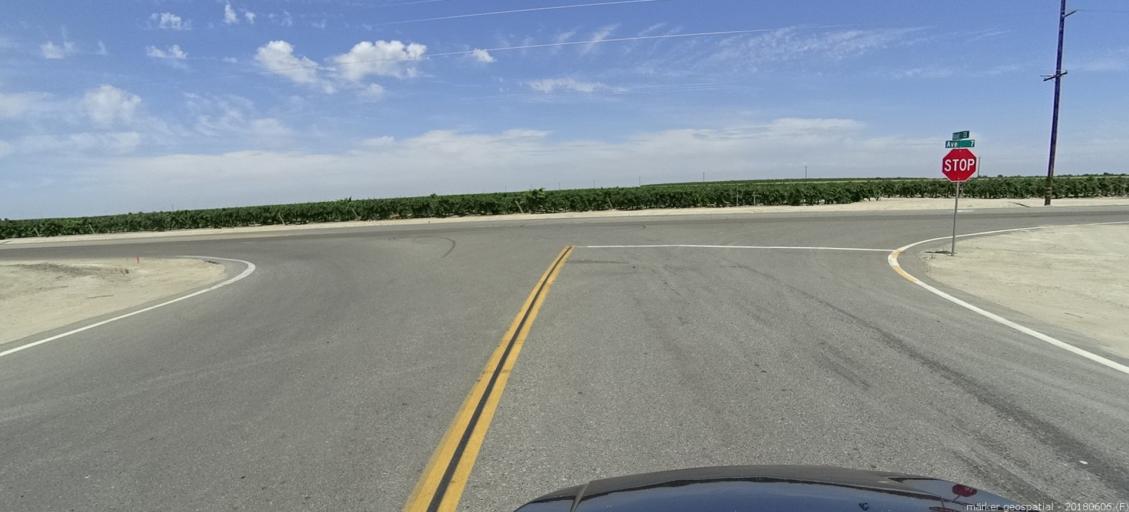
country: US
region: California
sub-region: Fresno County
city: Mendota
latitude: 36.8519
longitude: -120.3206
